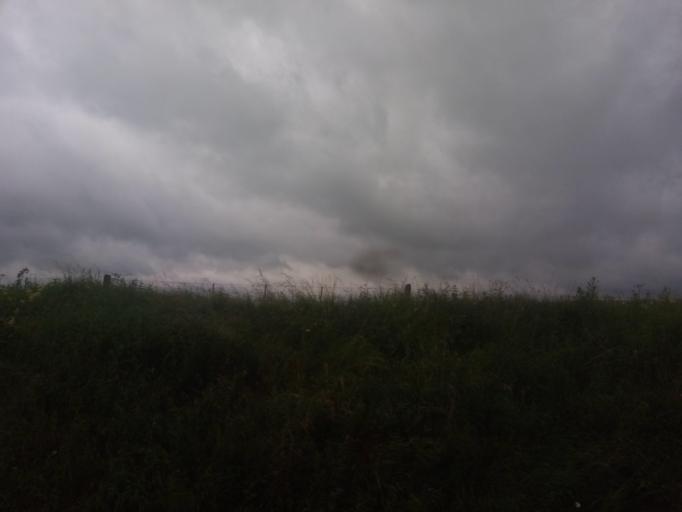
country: GB
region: England
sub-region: North Yorkshire
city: Settle
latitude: 54.0292
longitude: -2.2776
